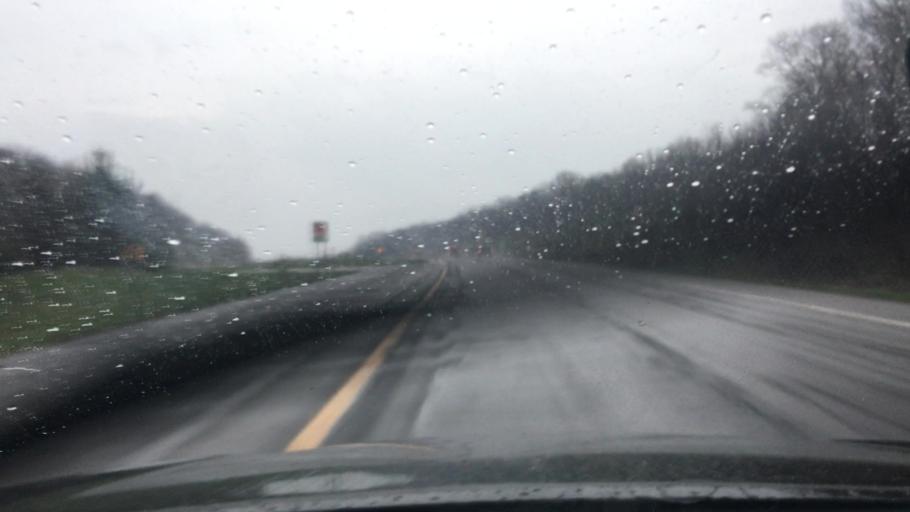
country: US
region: New York
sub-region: Chautauqua County
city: Lakewood
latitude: 42.1344
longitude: -79.3322
